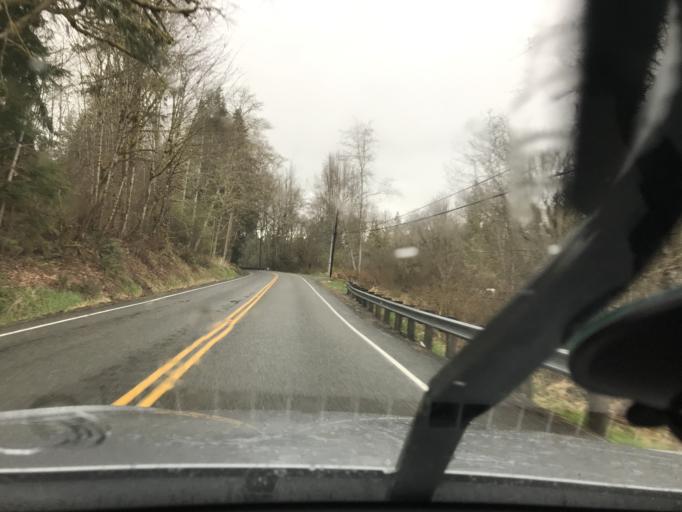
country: US
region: Washington
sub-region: King County
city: Ames Lake
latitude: 47.6552
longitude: -121.9637
